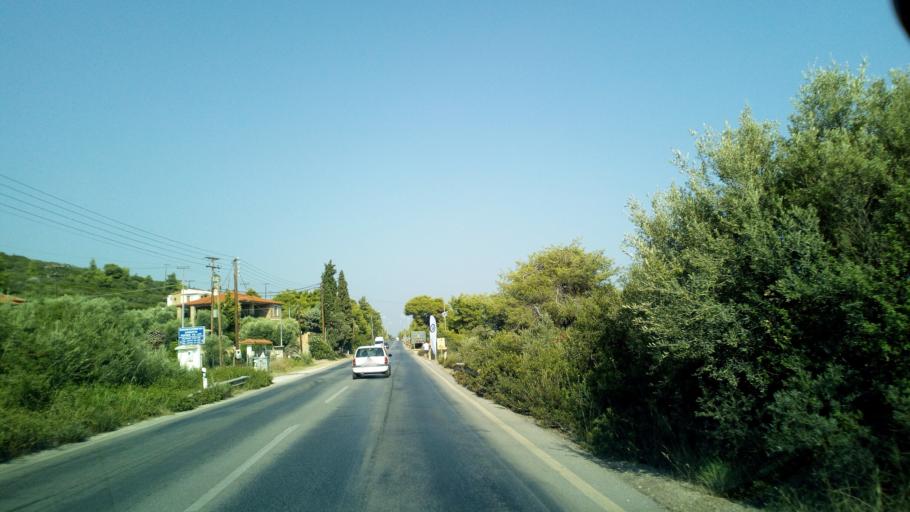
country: GR
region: Central Macedonia
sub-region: Nomos Chalkidikis
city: Ormylia
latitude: 40.2606
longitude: 23.4811
